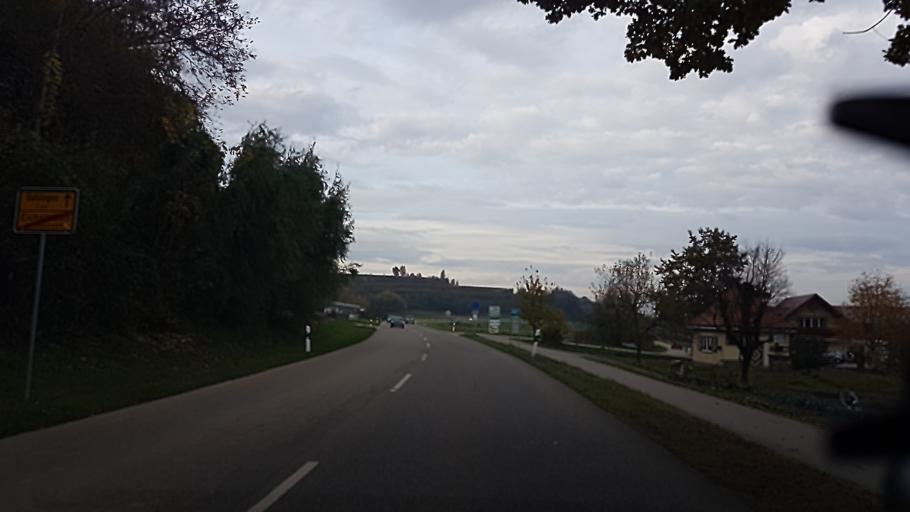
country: DE
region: Baden-Wuerttemberg
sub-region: Freiburg Region
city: Eichstetten
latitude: 48.0977
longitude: 7.7454
